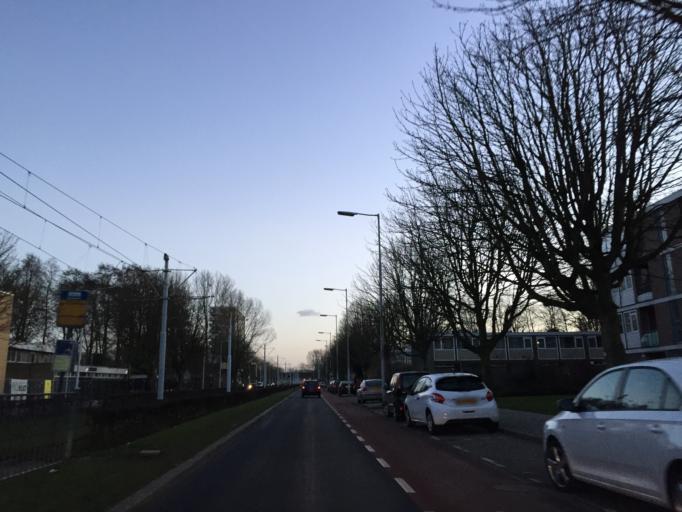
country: NL
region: South Holland
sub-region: Gemeente Rotterdam
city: Rotterdam
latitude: 51.9536
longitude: 4.4686
